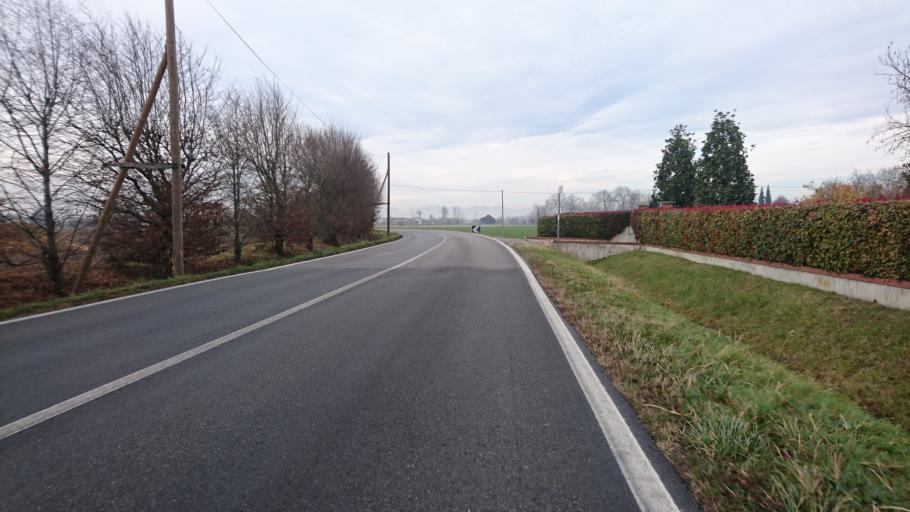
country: IT
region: Veneto
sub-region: Provincia di Padova
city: Villafranca Padovana
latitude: 45.4812
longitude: 11.7737
